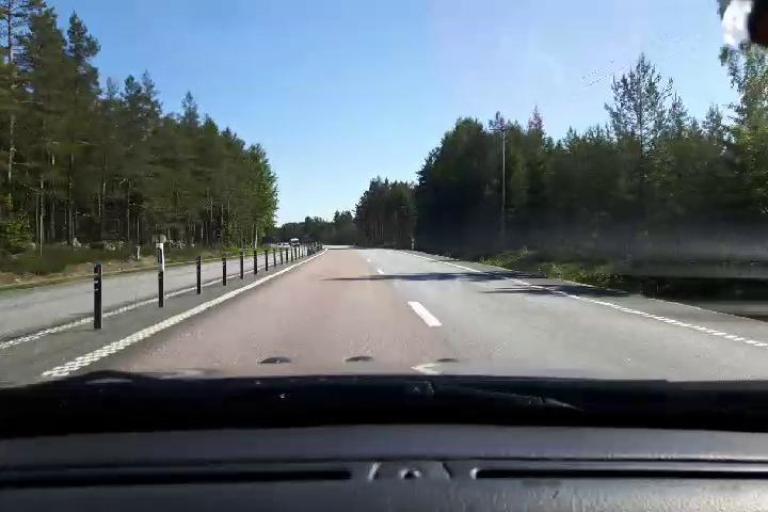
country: SE
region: Gaevleborg
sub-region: Gavle Kommun
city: Norrsundet
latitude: 61.0207
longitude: 16.9767
